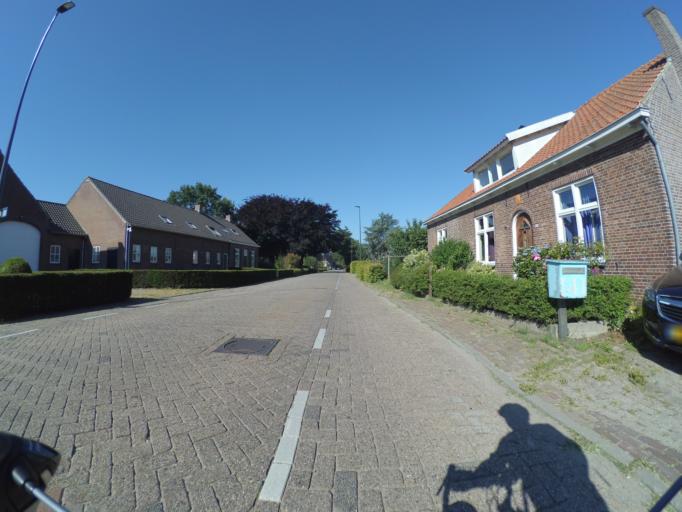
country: NL
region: North Brabant
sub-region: Gemeente Dongen
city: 's Gravenmoer
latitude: 51.6486
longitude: 4.9131
